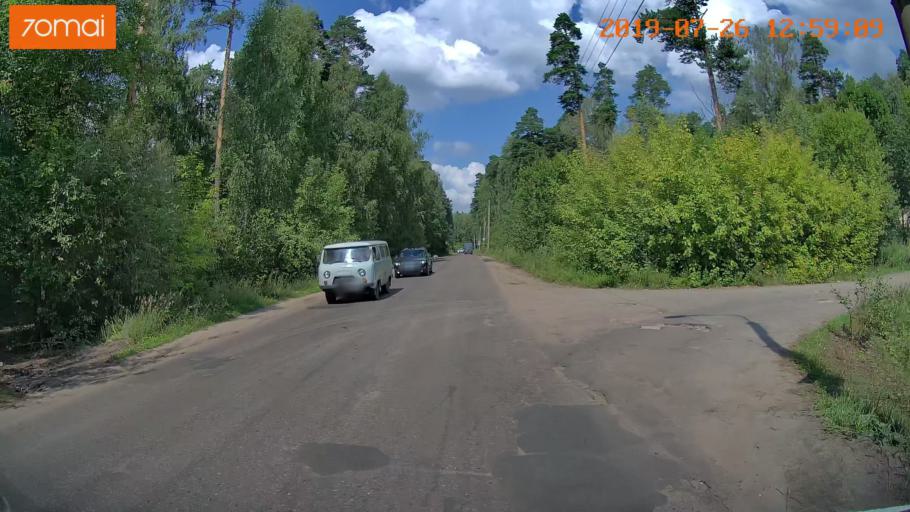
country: RU
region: Ivanovo
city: Bogorodskoye
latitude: 57.0272
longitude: 41.0208
